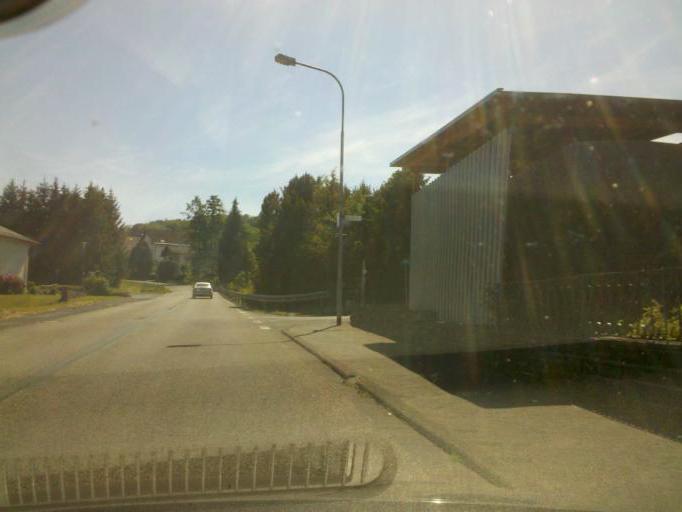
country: DE
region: Hesse
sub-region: Regierungsbezirk Giessen
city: Breitscheid
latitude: 50.7126
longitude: 8.1768
